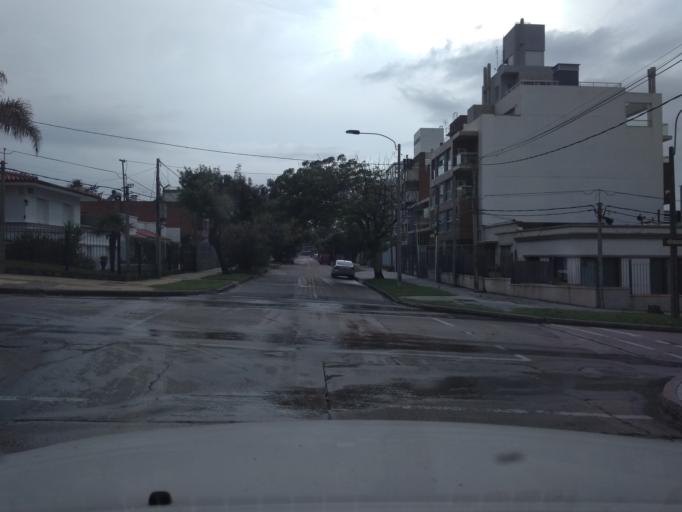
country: UY
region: Canelones
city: Paso de Carrasco
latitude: -34.8954
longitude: -56.0946
